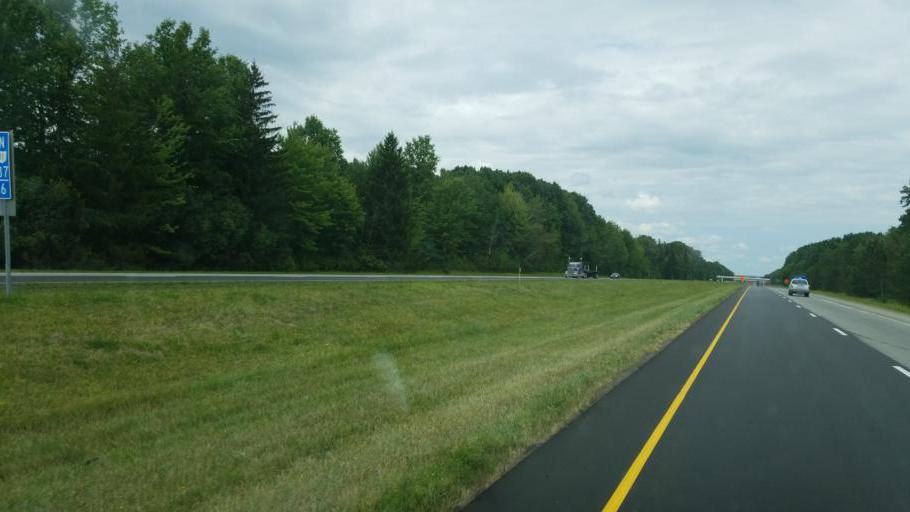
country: US
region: Ohio
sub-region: Mahoning County
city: Austintown
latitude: 41.0748
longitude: -80.7524
